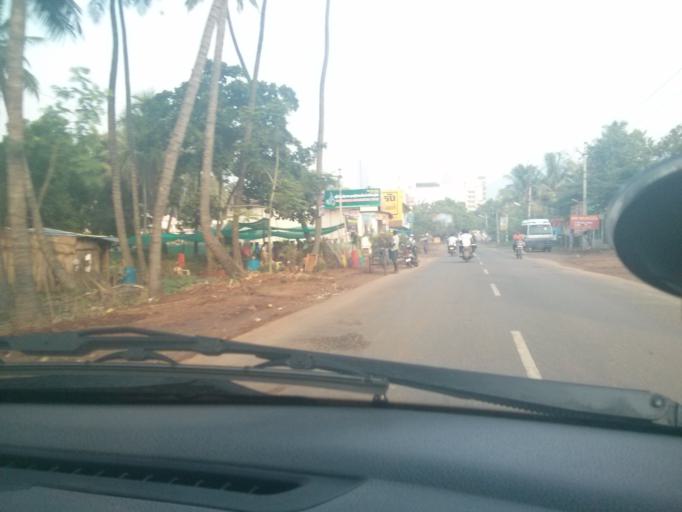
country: IN
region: Tamil Nadu
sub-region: Coimbatore
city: Perur
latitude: 11.0283
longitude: 76.8983
